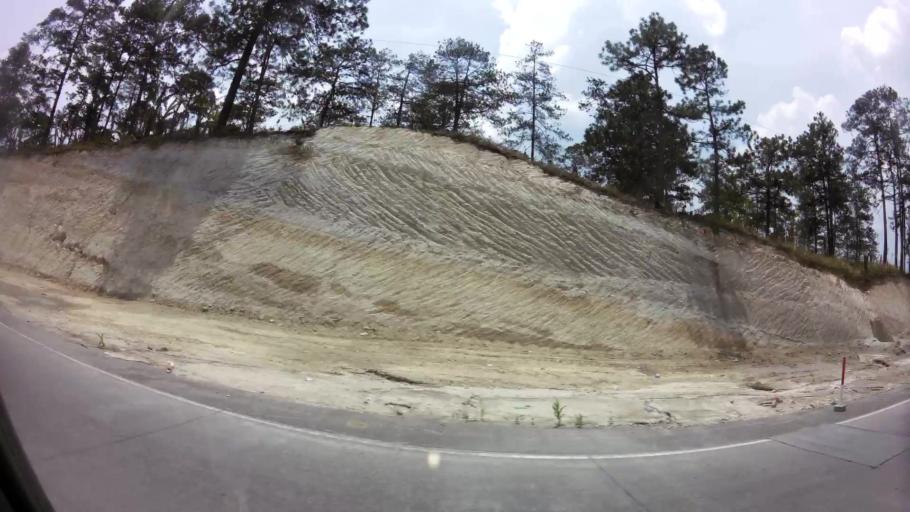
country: HN
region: Comayagua
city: El Socorro
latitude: 14.6433
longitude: -87.9265
